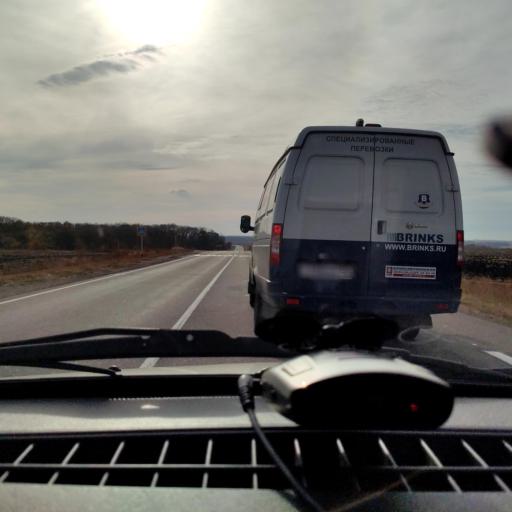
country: RU
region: Voronezj
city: Shilovo
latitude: 51.4599
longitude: 38.9704
